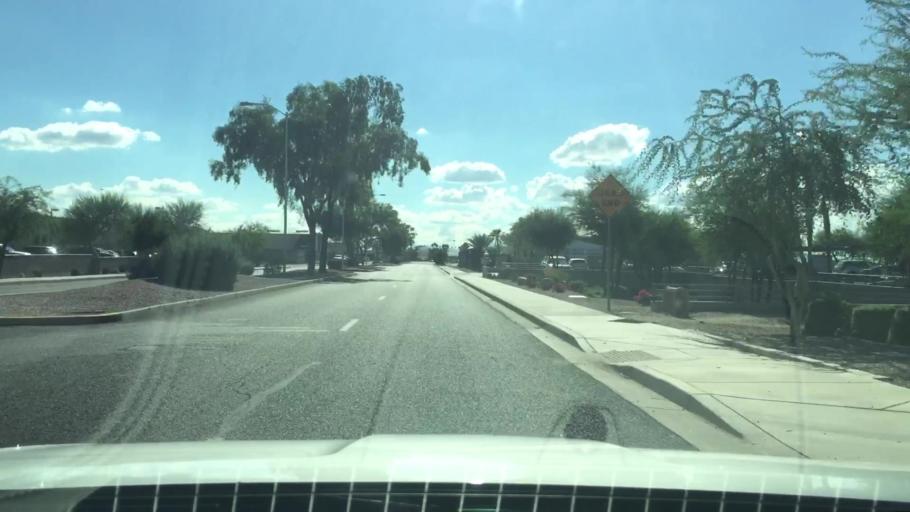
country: US
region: Arizona
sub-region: Maricopa County
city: Mesa
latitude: 33.4601
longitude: -111.7224
